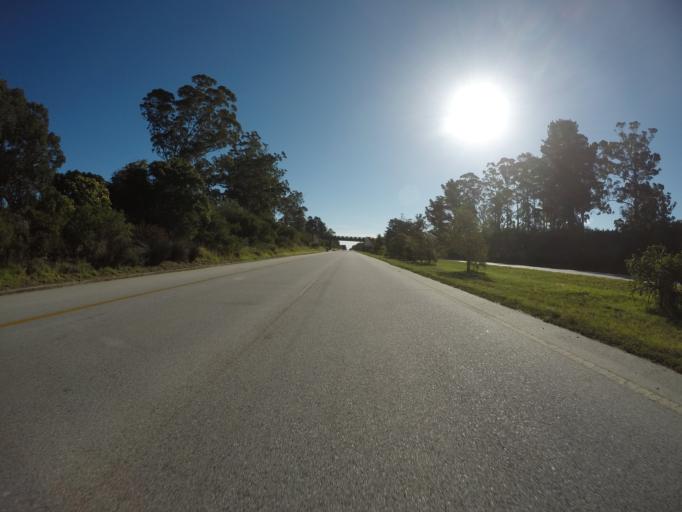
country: ZA
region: Eastern Cape
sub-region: Nelson Mandela Bay Metropolitan Municipality
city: Uitenhage
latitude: -33.9006
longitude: 25.1721
